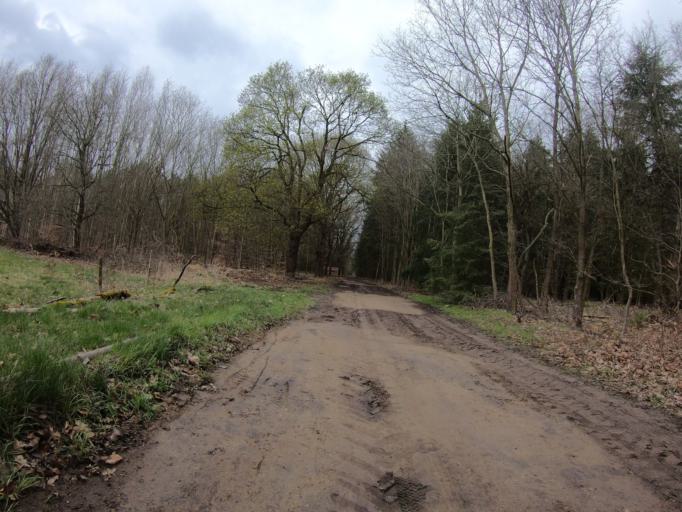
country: DE
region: Lower Saxony
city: Leiferde
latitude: 52.4826
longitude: 10.4568
